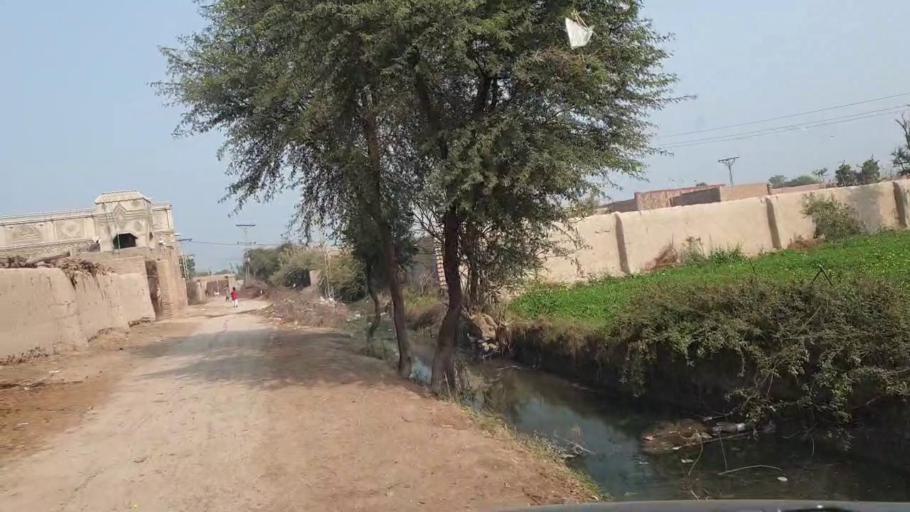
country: PK
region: Sindh
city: Bhit Shah
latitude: 25.8462
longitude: 68.4749
